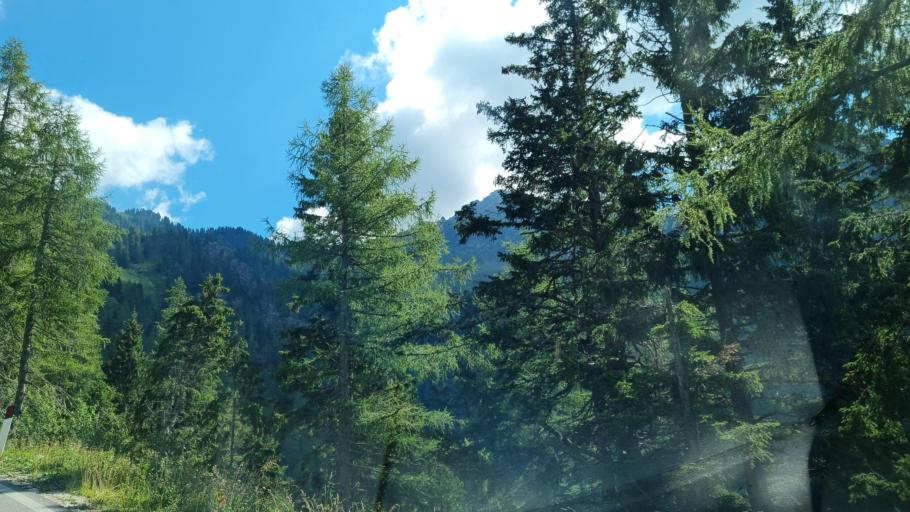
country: IT
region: Trentino-Alto Adige
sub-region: Provincia di Trento
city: Palu del Fersina
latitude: 46.1700
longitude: 11.4358
